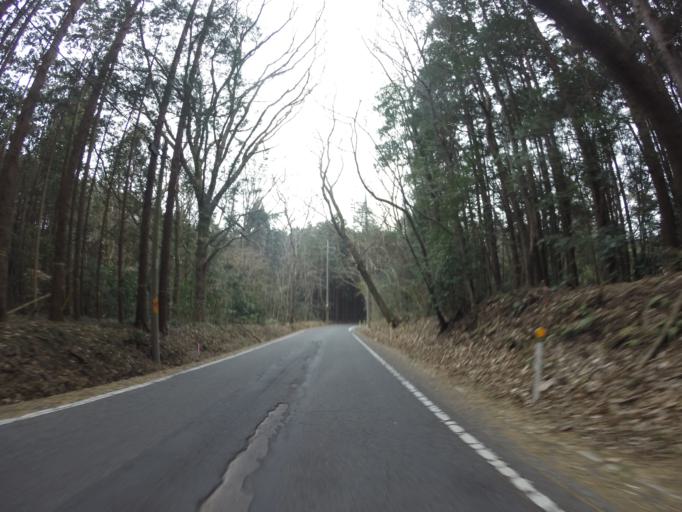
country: JP
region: Shizuoka
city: Fujinomiya
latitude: 35.2365
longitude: 138.5772
